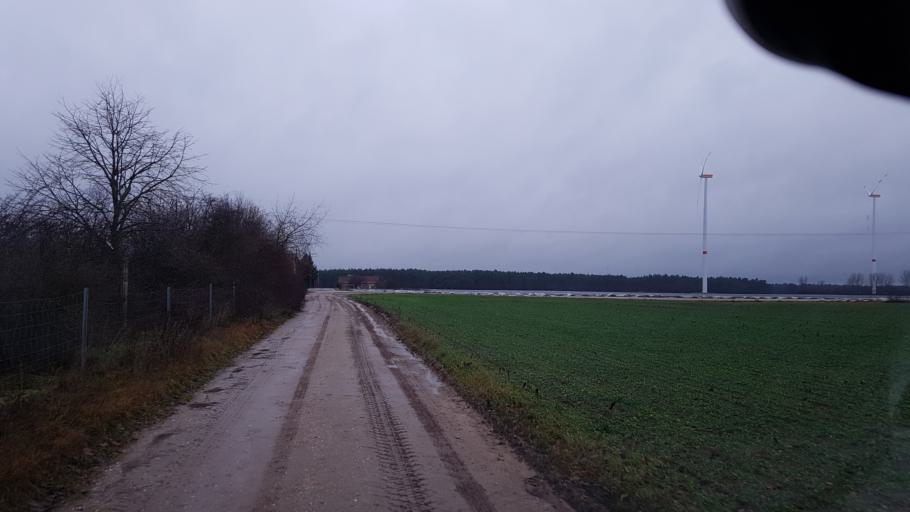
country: DE
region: Brandenburg
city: Sallgast
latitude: 51.6392
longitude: 13.8680
